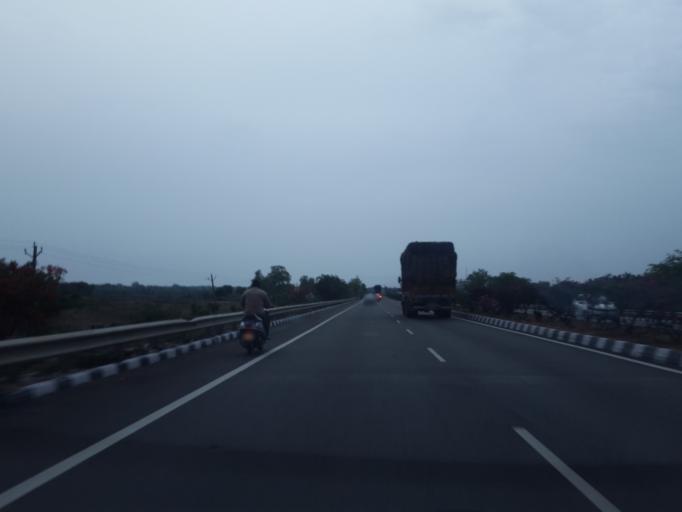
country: IN
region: Telangana
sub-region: Mahbubnagar
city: Farrukhnagar
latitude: 17.0807
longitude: 78.2306
